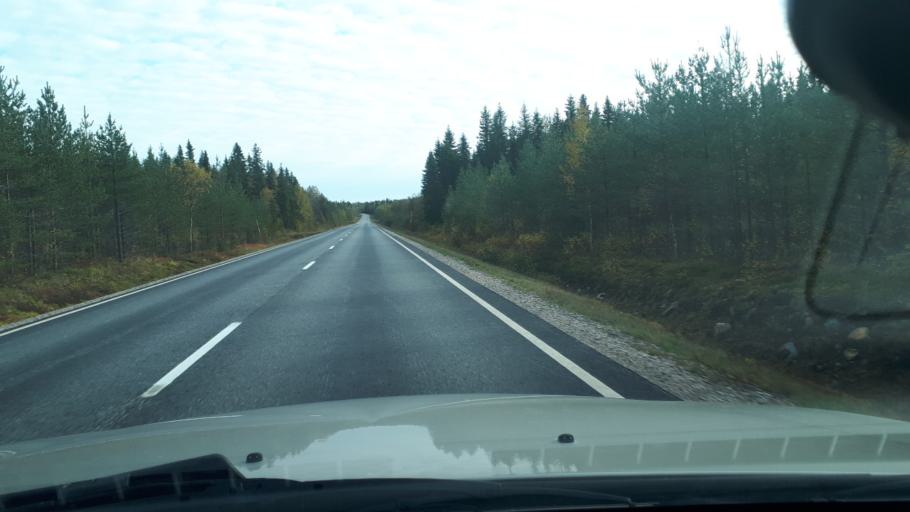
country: FI
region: Northern Ostrobothnia
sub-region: Oulu
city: Yli-Ii
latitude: 65.9258
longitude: 25.8289
